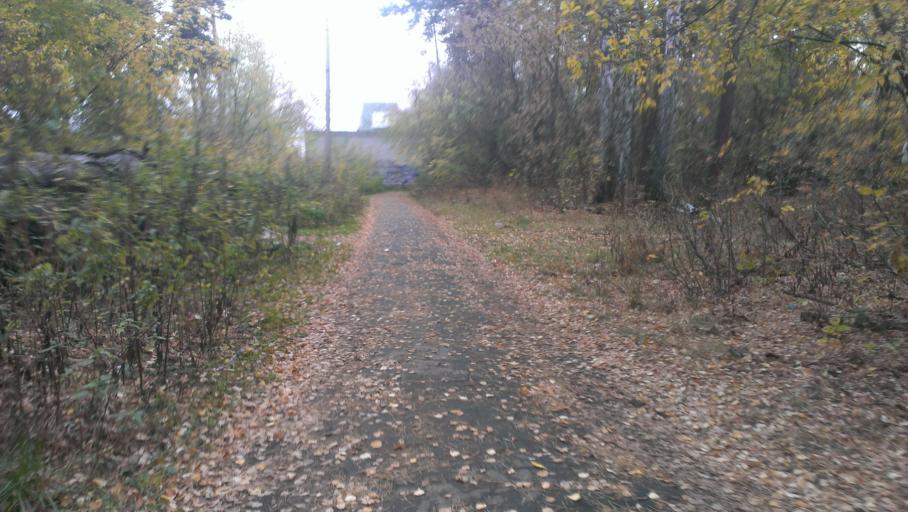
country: RU
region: Altai Krai
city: Yuzhnyy
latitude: 53.2588
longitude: 83.6897
